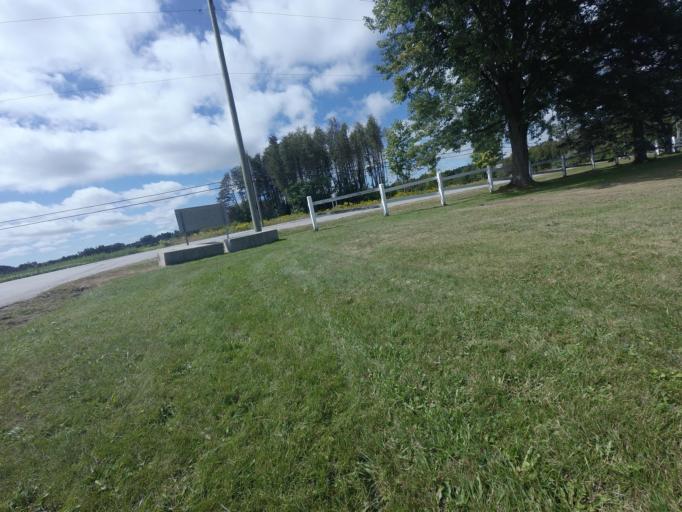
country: CA
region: Ontario
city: Uxbridge
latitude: 44.1252
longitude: -79.1272
